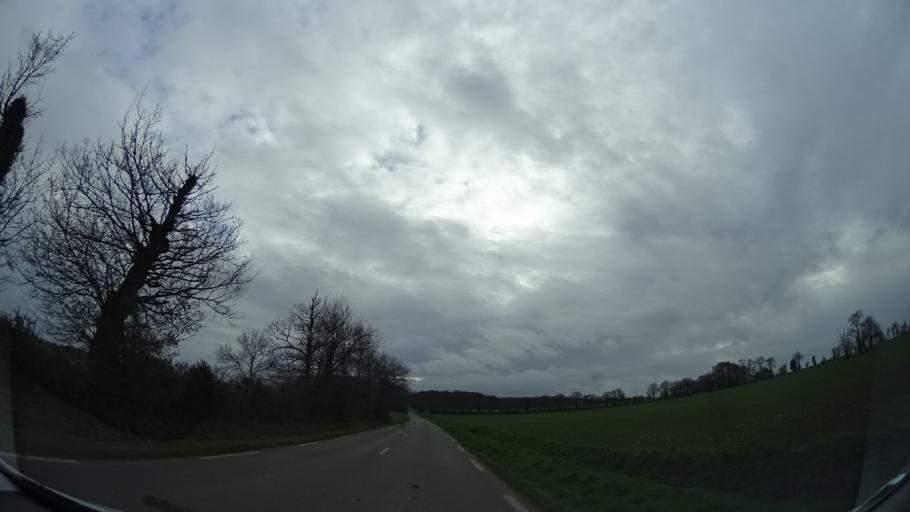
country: FR
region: Brittany
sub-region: Departement des Cotes-d'Armor
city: Evran
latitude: 48.3622
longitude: -1.9704
